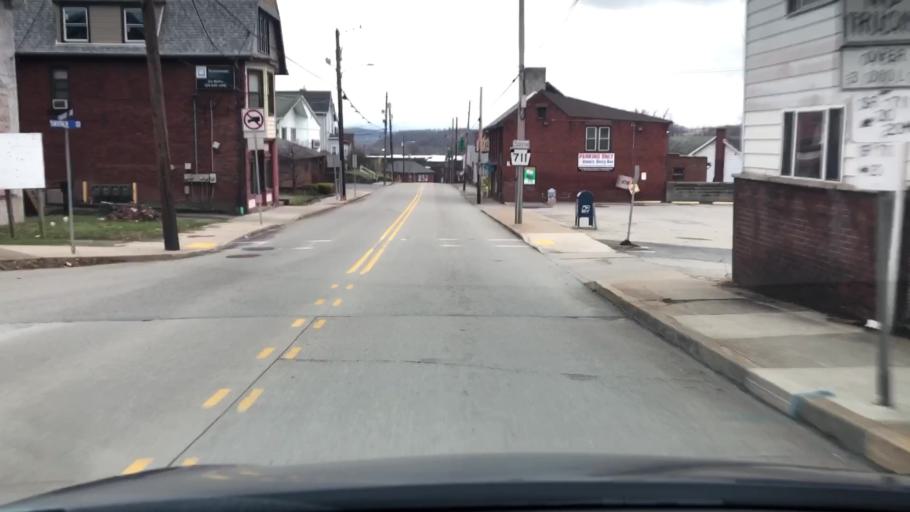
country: US
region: Pennsylvania
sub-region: Fayette County
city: Connellsville
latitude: 40.0200
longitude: -79.5844
